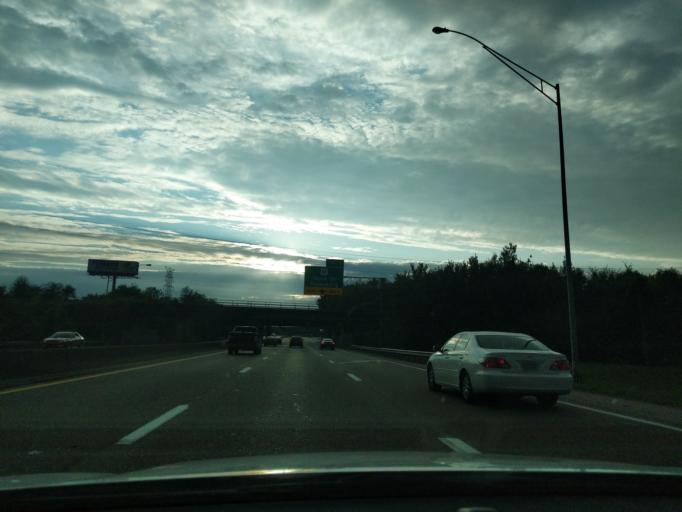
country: US
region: Tennessee
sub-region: Shelby County
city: New South Memphis
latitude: 35.0782
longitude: -90.0508
